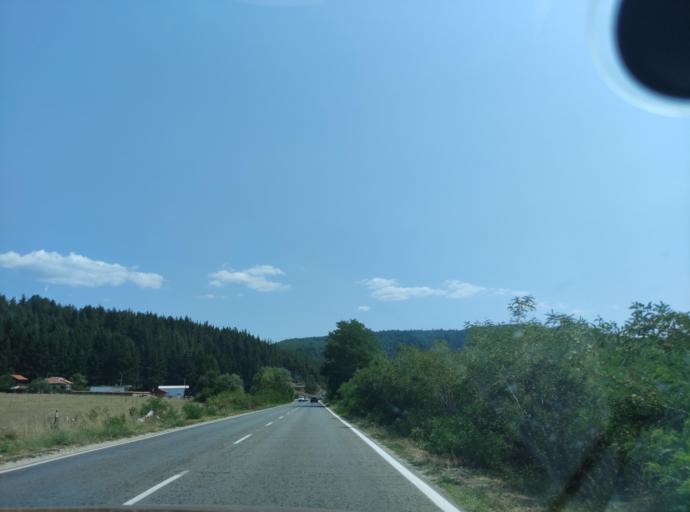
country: BG
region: Blagoevgrad
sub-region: Obshtina Razlog
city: Razlog
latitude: 41.8886
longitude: 23.5233
